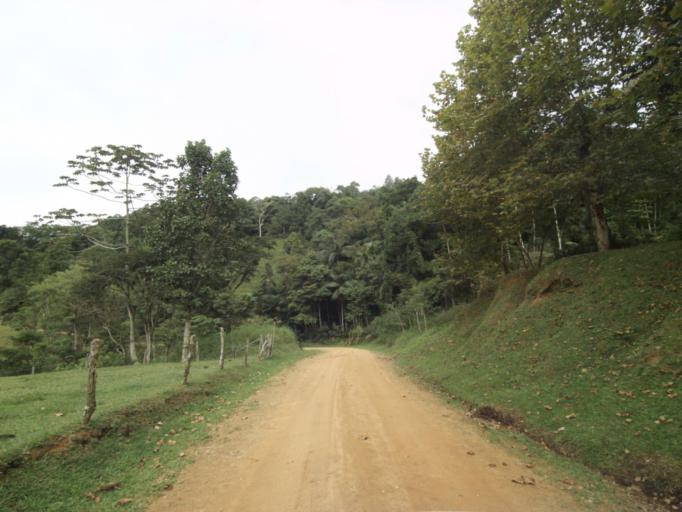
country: BR
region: Santa Catarina
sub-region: Pomerode
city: Pomerode
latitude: -26.7368
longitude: -49.1977
